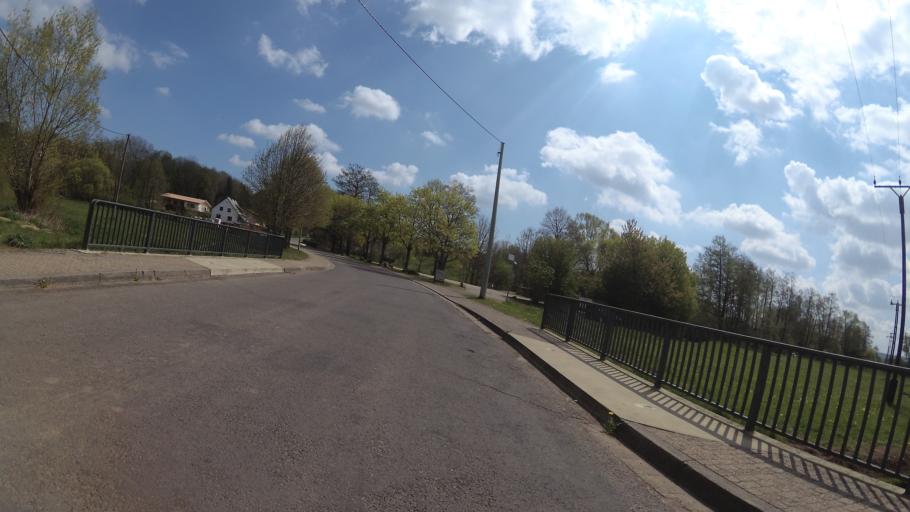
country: DE
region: Saarland
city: Wadern
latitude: 49.5587
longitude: 6.8929
